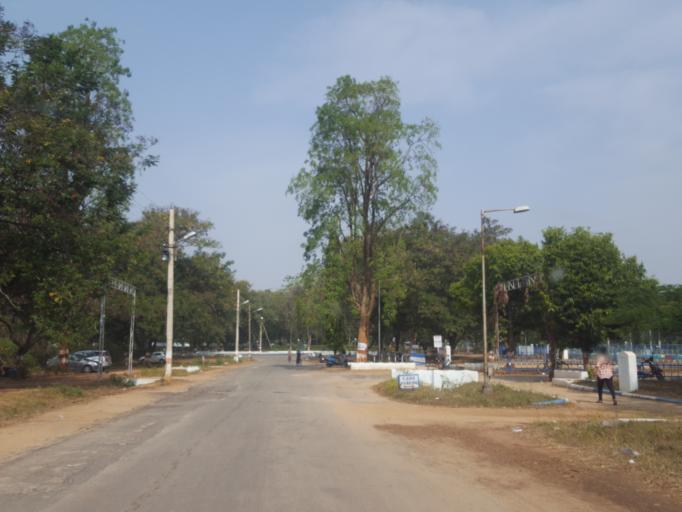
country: IN
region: Telangana
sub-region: Medak
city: Serilingampalle
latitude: 17.4932
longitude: 78.3071
